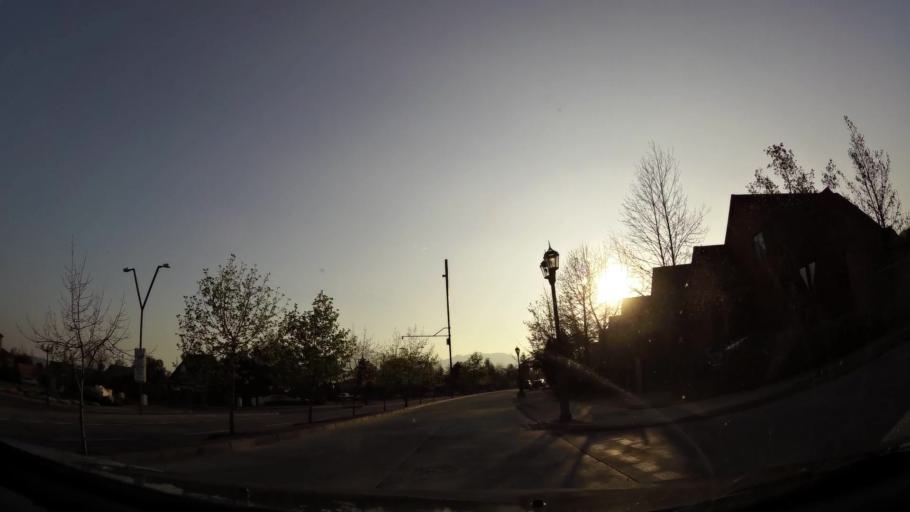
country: CL
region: Santiago Metropolitan
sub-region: Provincia de Chacabuco
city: Chicureo Abajo
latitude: -33.3266
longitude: -70.5132
